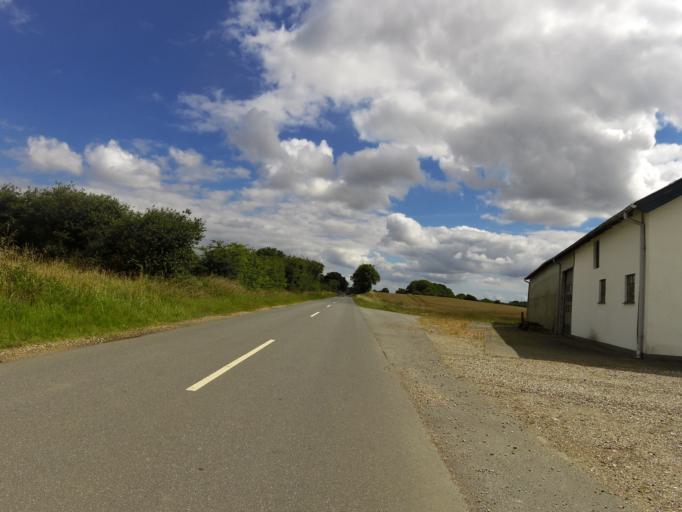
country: DK
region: South Denmark
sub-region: Haderslev Kommune
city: Vojens
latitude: 55.2840
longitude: 9.3770
